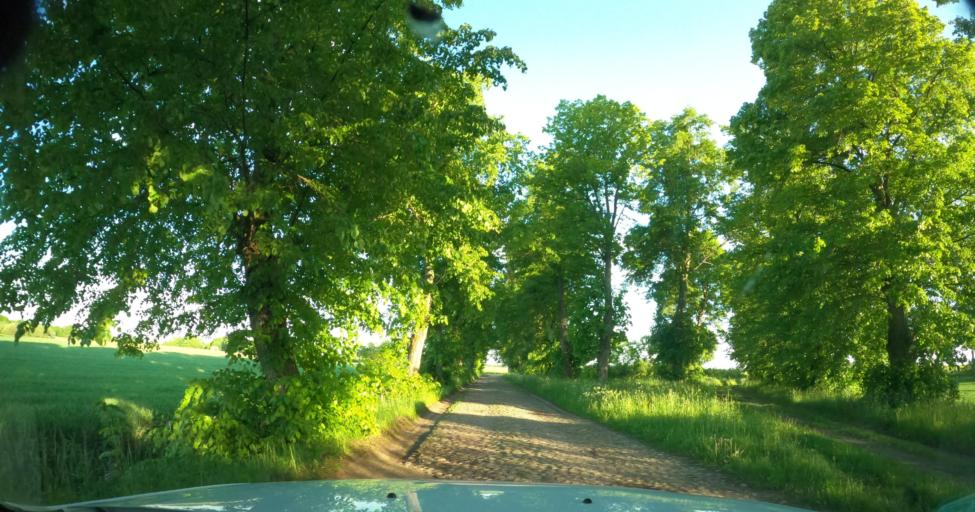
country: PL
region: Warmian-Masurian Voivodeship
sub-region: Powiat braniewski
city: Pieniezno
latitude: 54.1792
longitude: 20.1347
